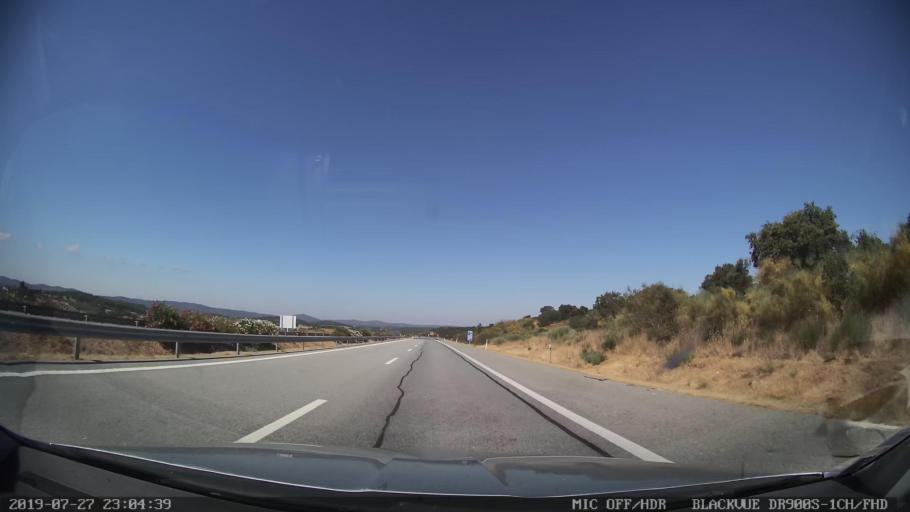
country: PT
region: Evora
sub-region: Estremoz
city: Estremoz
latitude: 38.8228
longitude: -7.5915
